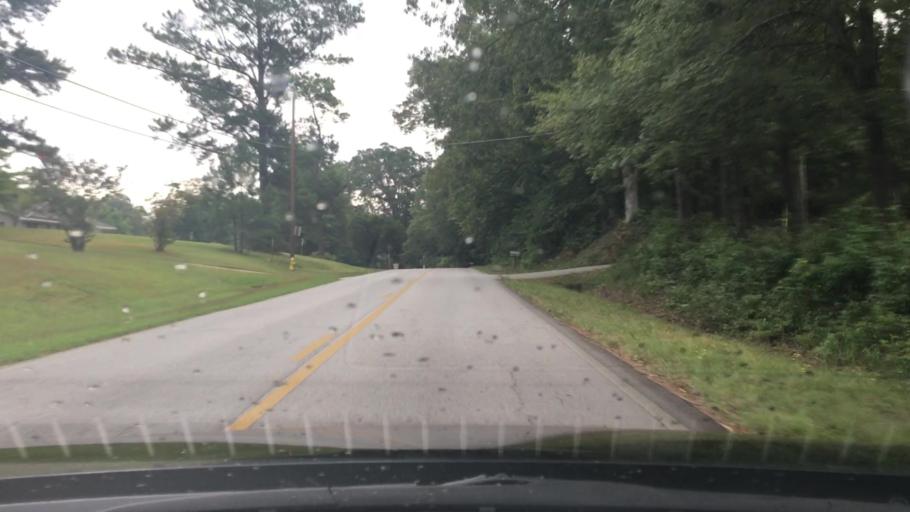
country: US
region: Georgia
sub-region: Spalding County
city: Experiment
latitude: 33.2802
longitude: -84.3851
